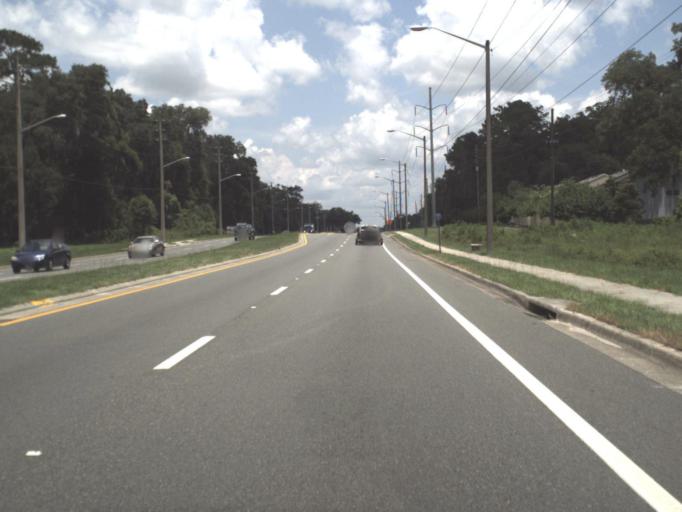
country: US
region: Florida
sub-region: Alachua County
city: Gainesville
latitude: 29.6117
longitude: -82.3968
